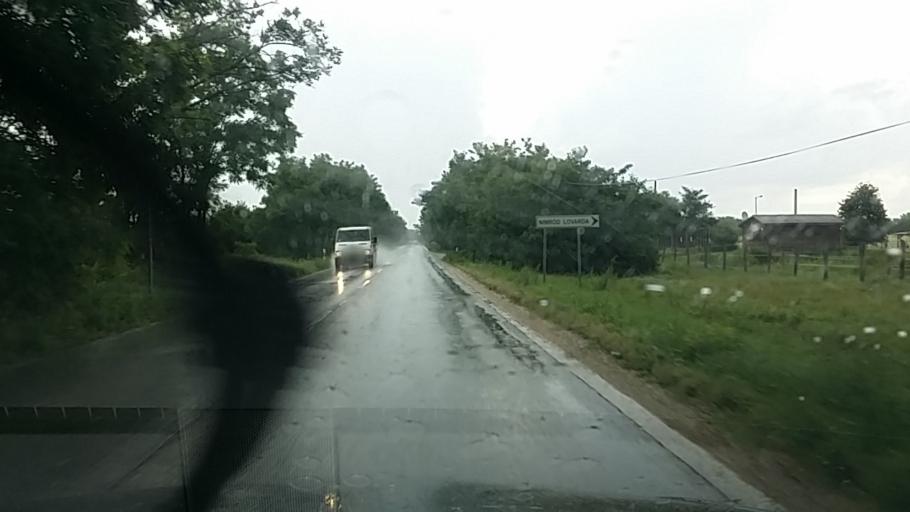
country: HU
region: Pest
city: Ocsa
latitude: 47.3089
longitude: 19.2848
